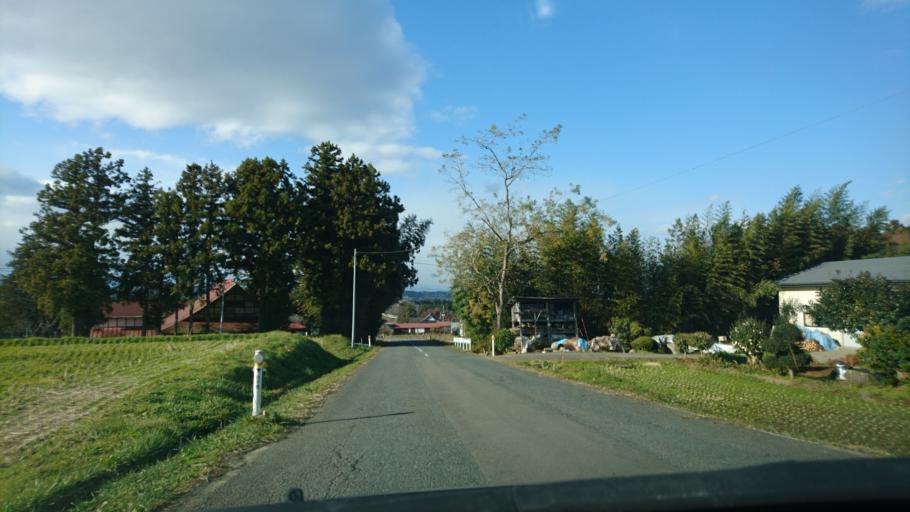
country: JP
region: Iwate
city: Mizusawa
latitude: 39.0339
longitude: 141.1546
